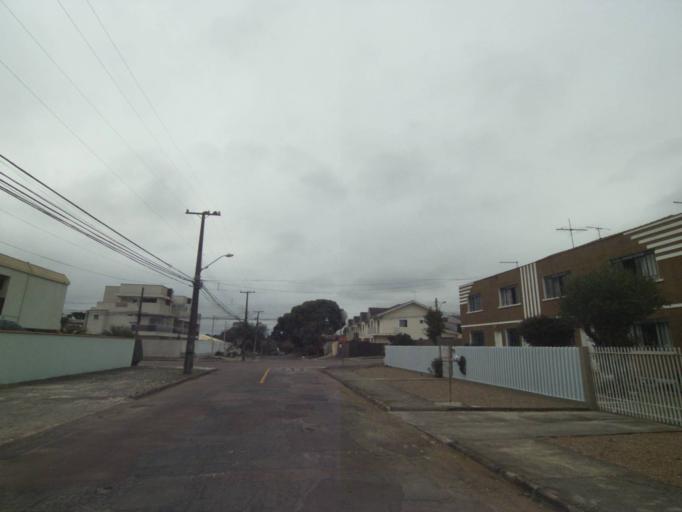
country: BR
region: Parana
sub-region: Pinhais
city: Pinhais
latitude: -25.4808
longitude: -49.2309
